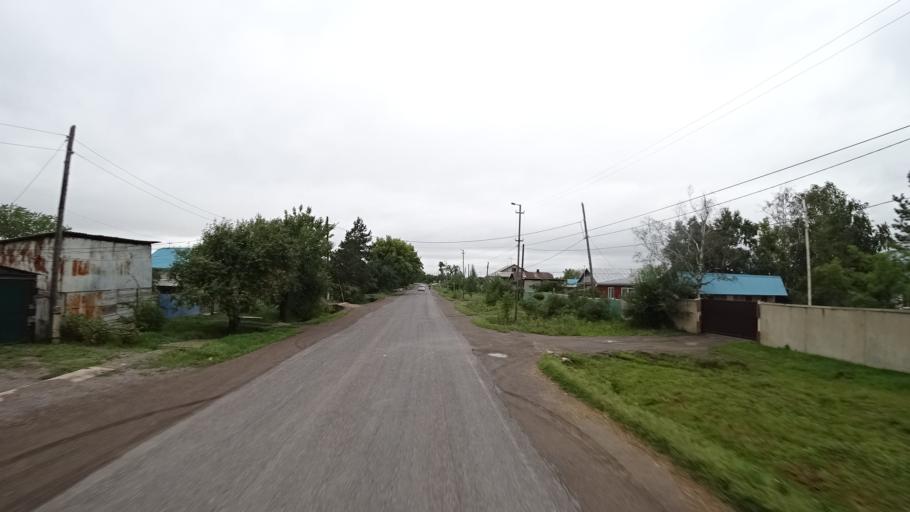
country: RU
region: Primorskiy
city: Chernigovka
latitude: 44.3461
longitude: 132.5658
